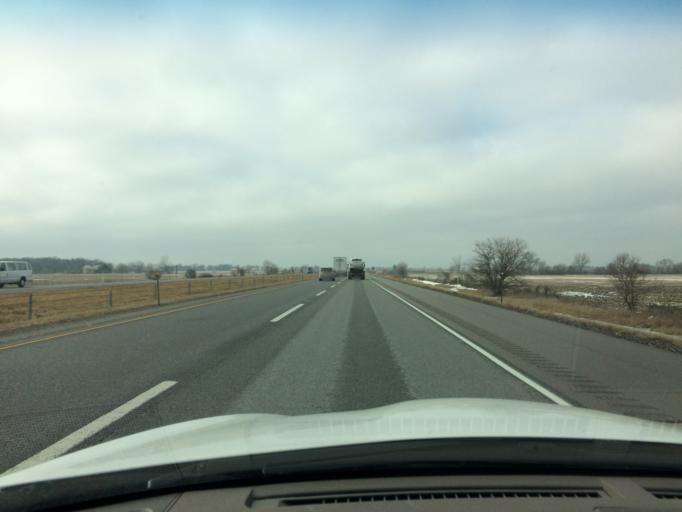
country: US
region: Illinois
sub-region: Kane County
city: Maple Park
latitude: 41.8609
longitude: -88.5455
